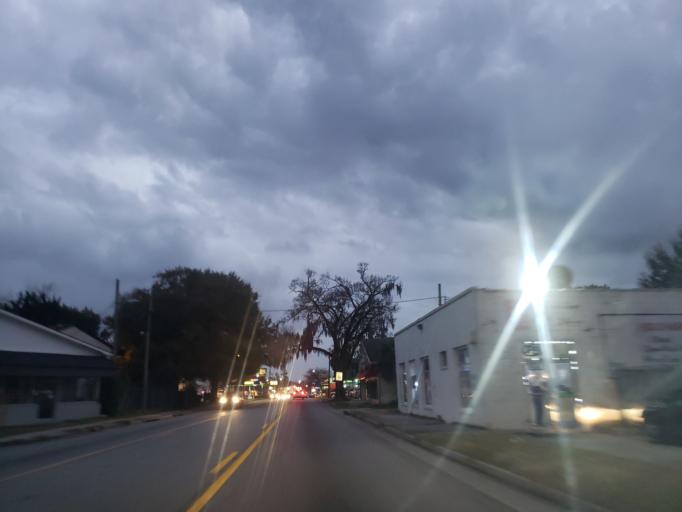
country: US
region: Georgia
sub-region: Chatham County
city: Thunderbolt
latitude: 32.0461
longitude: -81.0642
